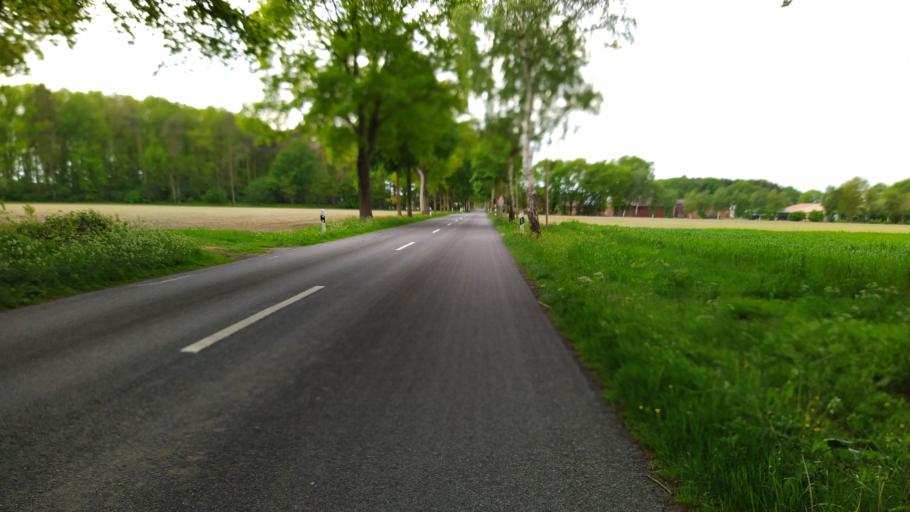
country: DE
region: Lower Saxony
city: Farven
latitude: 53.4258
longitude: 9.3036
